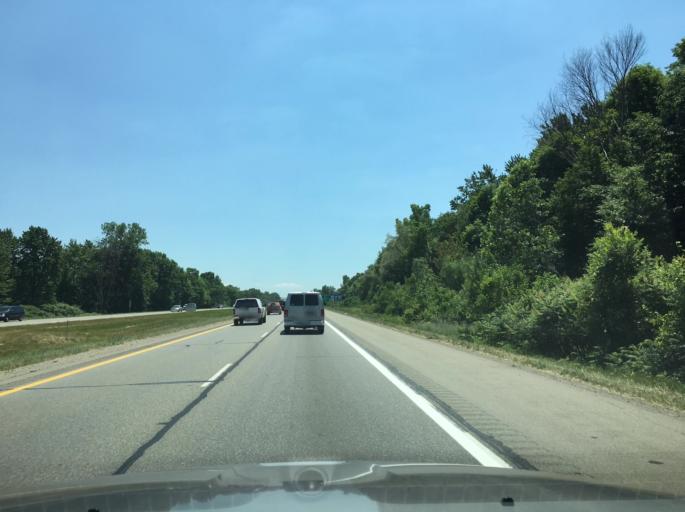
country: US
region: Michigan
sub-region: Macomb County
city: Shelby
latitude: 42.6483
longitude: -83.0141
